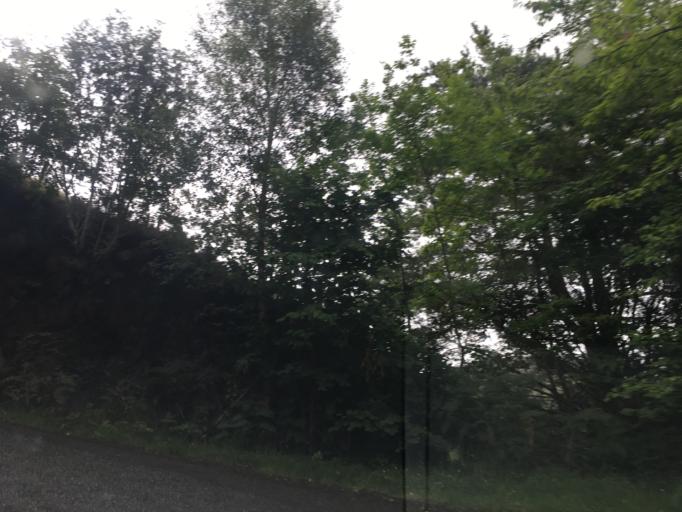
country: GB
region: Scotland
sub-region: Argyll and Bute
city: Oban
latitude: 56.2603
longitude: -5.4715
